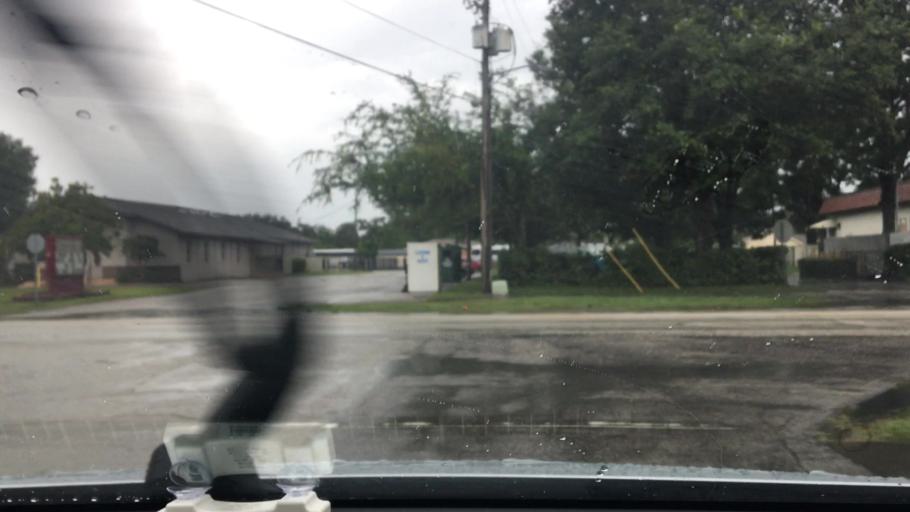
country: US
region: Florida
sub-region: Volusia County
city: Deltona
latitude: 28.8812
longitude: -81.2407
